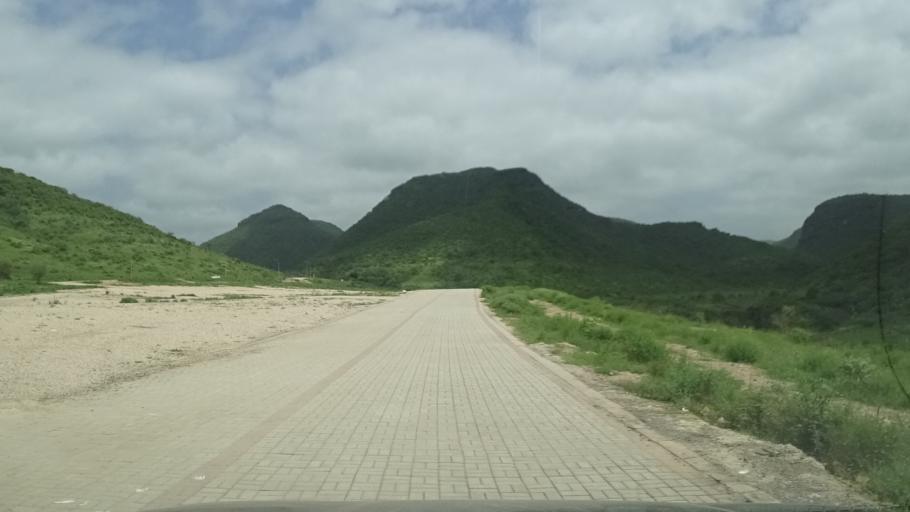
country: OM
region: Zufar
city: Salalah
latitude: 17.1458
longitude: 54.1778
